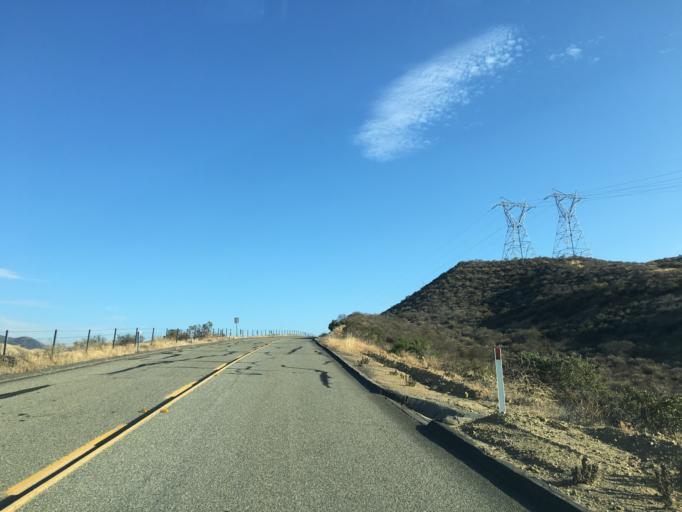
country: US
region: California
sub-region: Los Angeles County
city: Castaic
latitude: 34.5256
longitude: -118.6421
